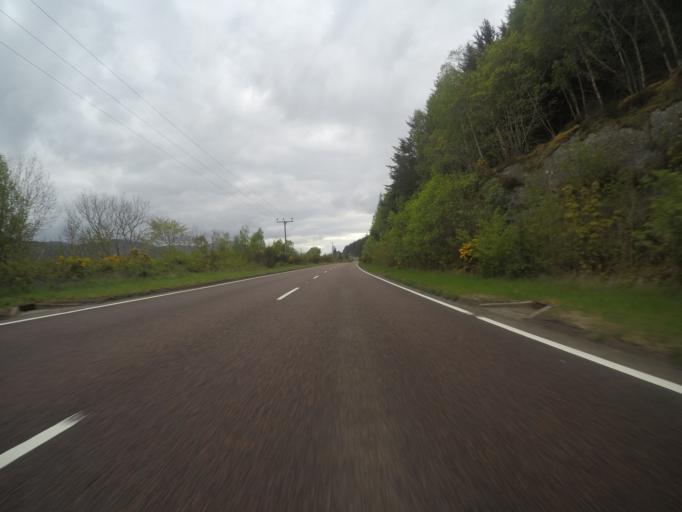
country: GB
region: Scotland
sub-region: Highland
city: Beauly
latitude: 57.2309
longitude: -4.5650
